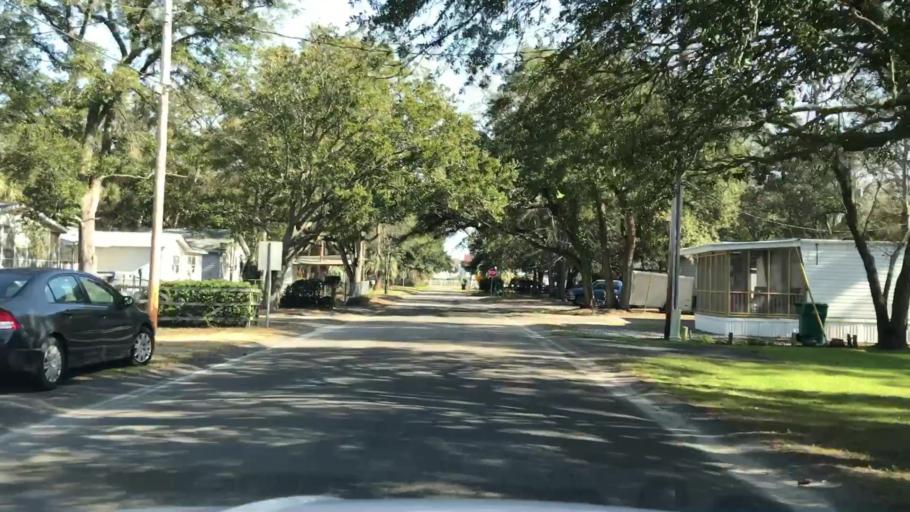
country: US
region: South Carolina
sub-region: Horry County
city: Garden City
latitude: 33.5858
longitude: -79.0021
